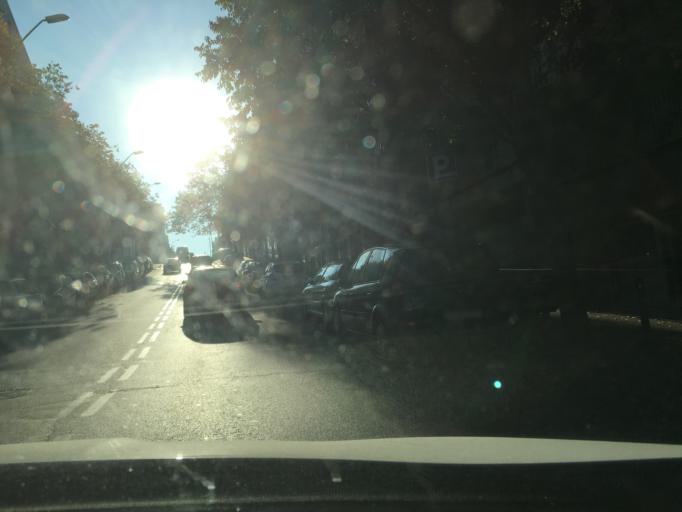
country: ES
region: Catalonia
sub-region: Provincia de Barcelona
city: Santa Coloma de Gramenet
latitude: 41.4557
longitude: 2.2094
